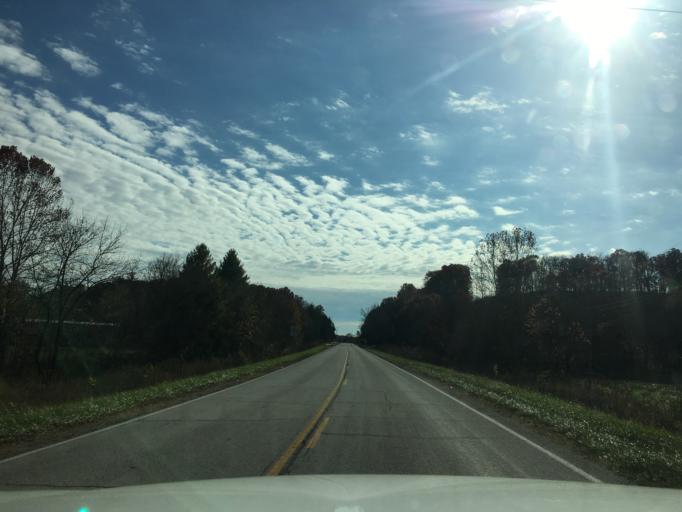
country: US
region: Missouri
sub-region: Osage County
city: Linn
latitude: 38.3948
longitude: -91.8241
